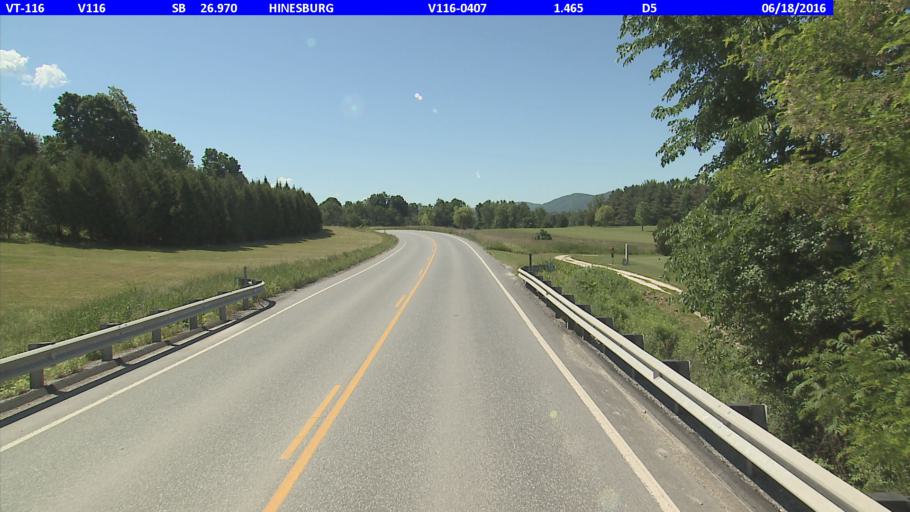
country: US
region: Vermont
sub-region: Chittenden County
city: Hinesburg
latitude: 44.3007
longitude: -73.0741
